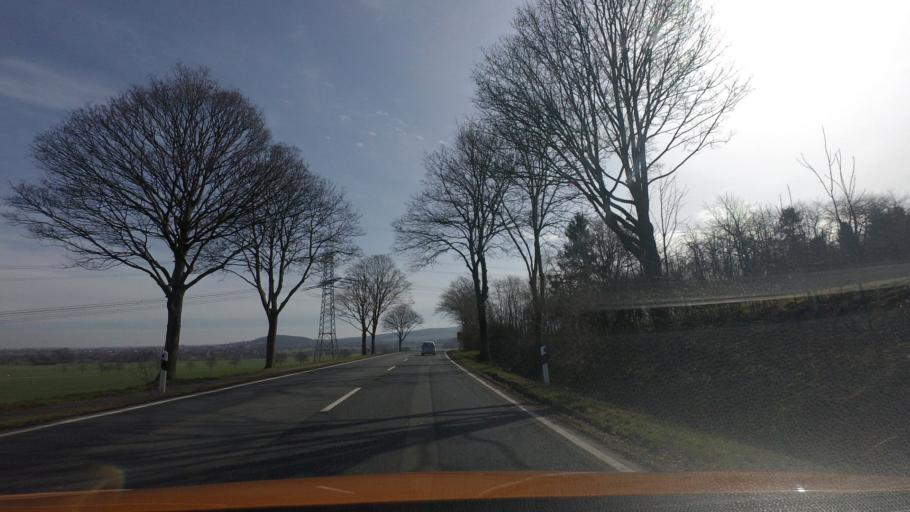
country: DE
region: Lower Saxony
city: Beckedorf
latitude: 52.3365
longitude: 9.3278
